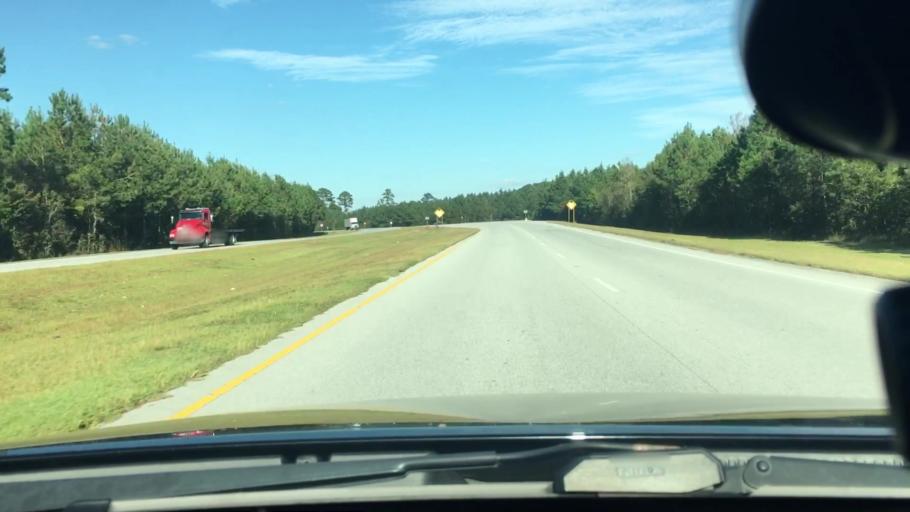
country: US
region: North Carolina
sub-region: Craven County
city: Trent Woods
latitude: 35.1390
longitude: -77.1121
